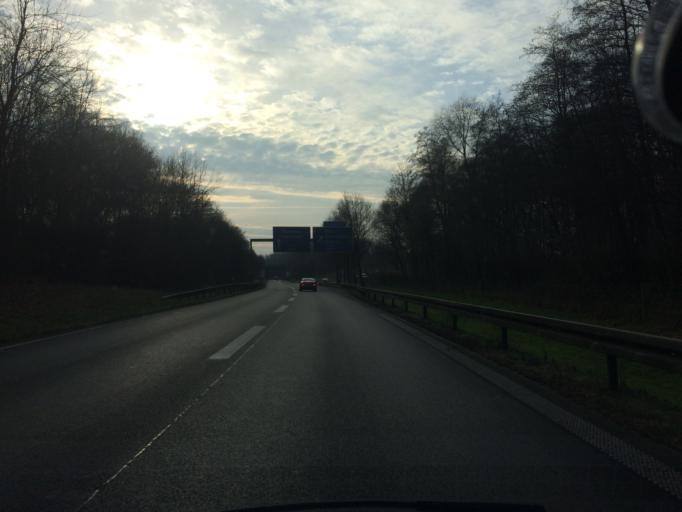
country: DE
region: North Rhine-Westphalia
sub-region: Regierungsbezirk Munster
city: Bottrop
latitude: 51.5582
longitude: 6.9264
